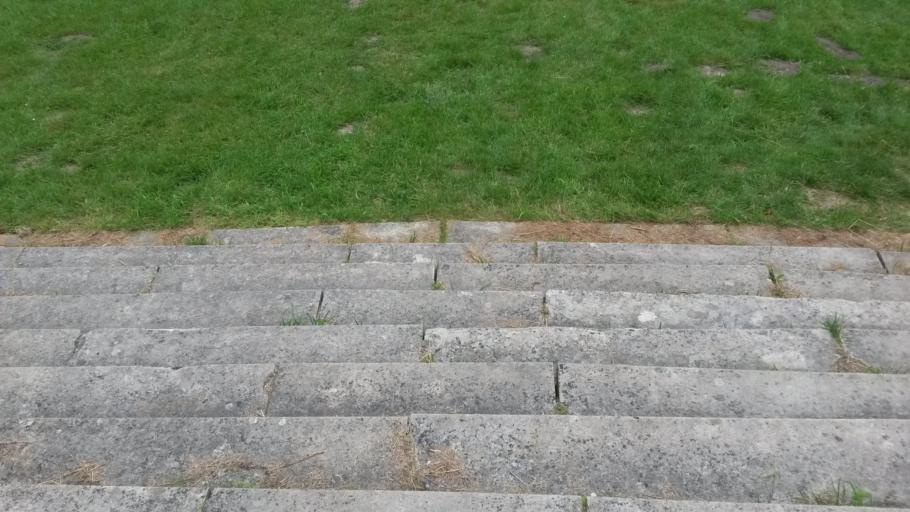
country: FR
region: Ile-de-France
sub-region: Departement de Seine-et-Marne
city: Champs-sur-Marne
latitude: 48.8600
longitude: 2.6035
